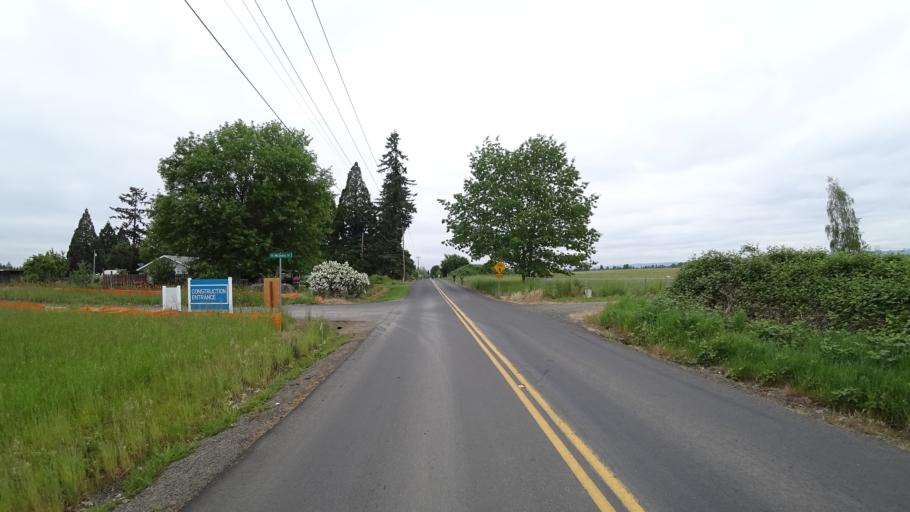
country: US
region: Oregon
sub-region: Washington County
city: Aloha
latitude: 45.4866
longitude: -122.9127
